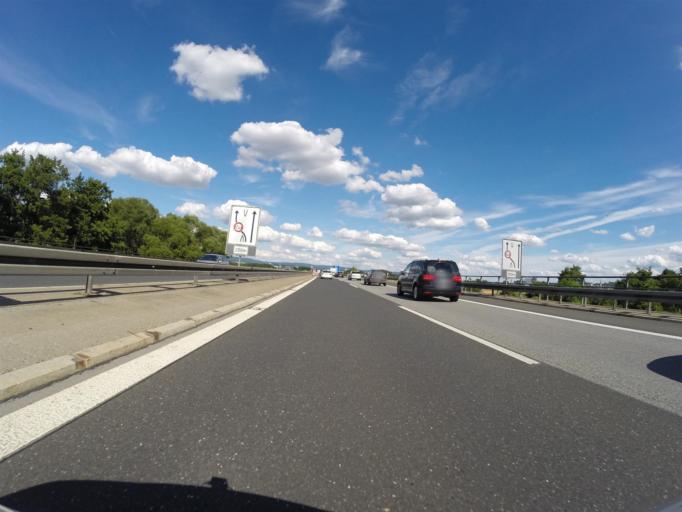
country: DE
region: Bavaria
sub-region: Upper Franconia
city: Bischberg
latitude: 49.9179
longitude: 10.8448
